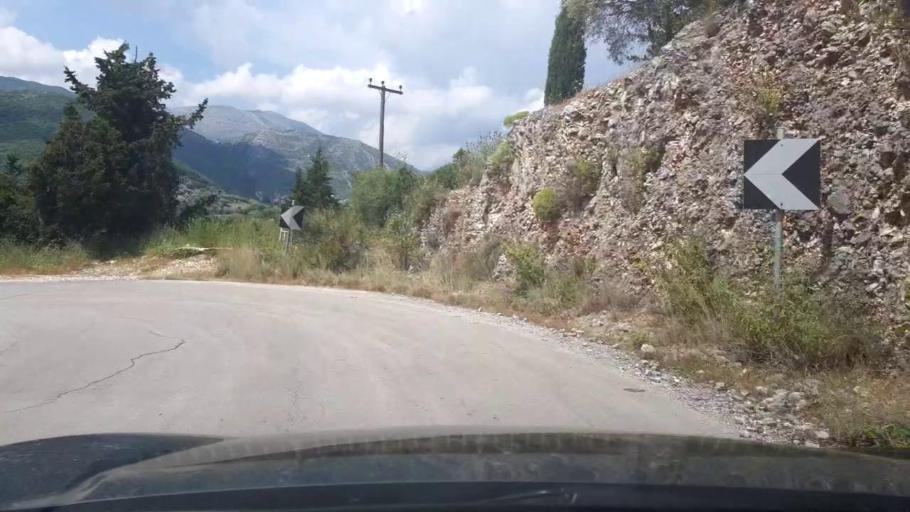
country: GR
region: Ionian Islands
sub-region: Lefkada
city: Nidri
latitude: 38.6489
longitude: 20.7037
